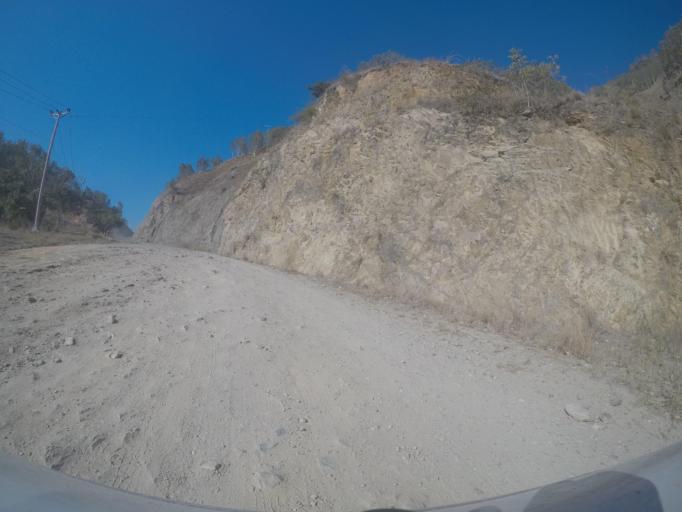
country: TL
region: Dili
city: Dili
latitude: -8.5314
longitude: 125.6198
